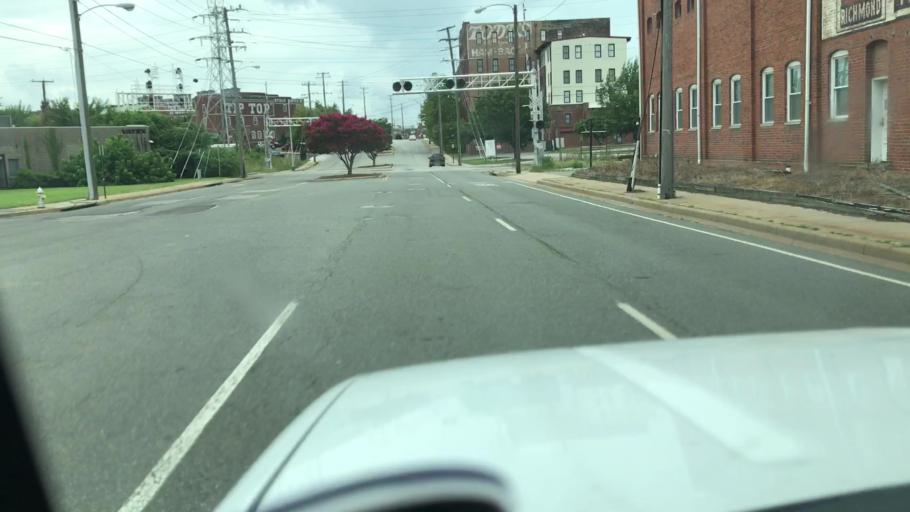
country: US
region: Virginia
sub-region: City of Richmond
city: Richmond
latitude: 37.5638
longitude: -77.4605
